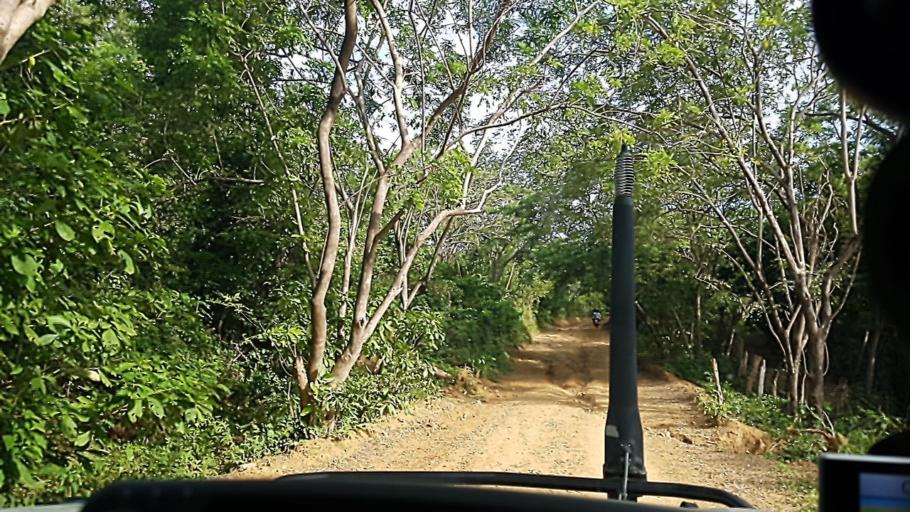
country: NI
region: Rivas
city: Tola
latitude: 11.5188
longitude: -86.1372
